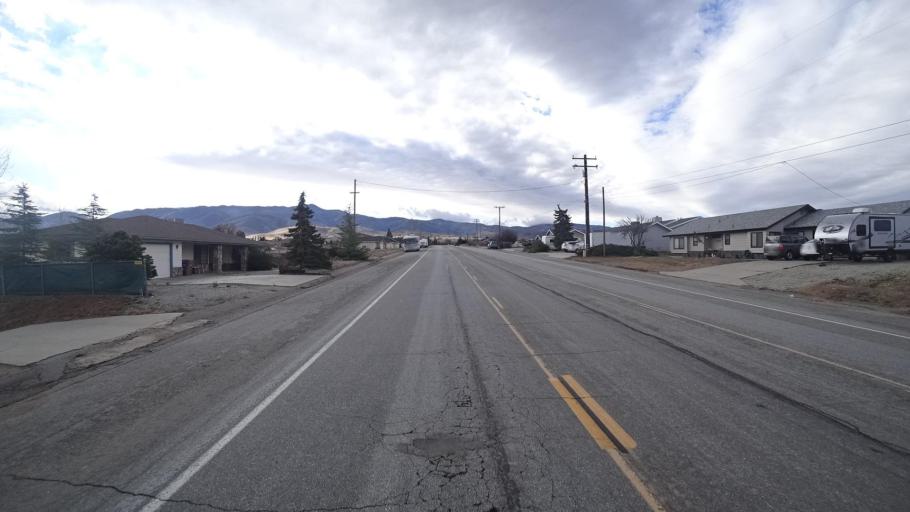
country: US
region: California
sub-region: Kern County
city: Golden Hills
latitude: 35.1323
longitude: -118.4813
